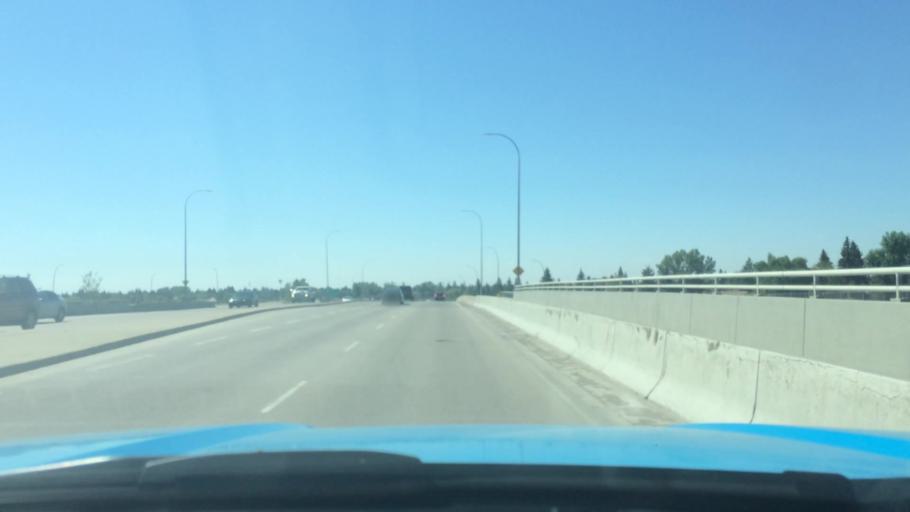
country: CA
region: Alberta
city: Calgary
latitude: 51.0672
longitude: -113.9585
